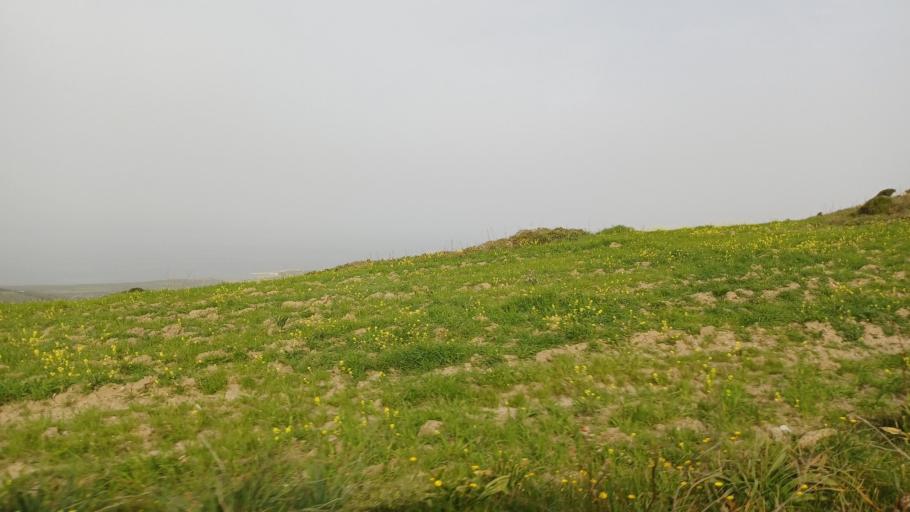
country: CY
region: Pafos
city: Pegeia
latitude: 34.9505
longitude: 32.3793
